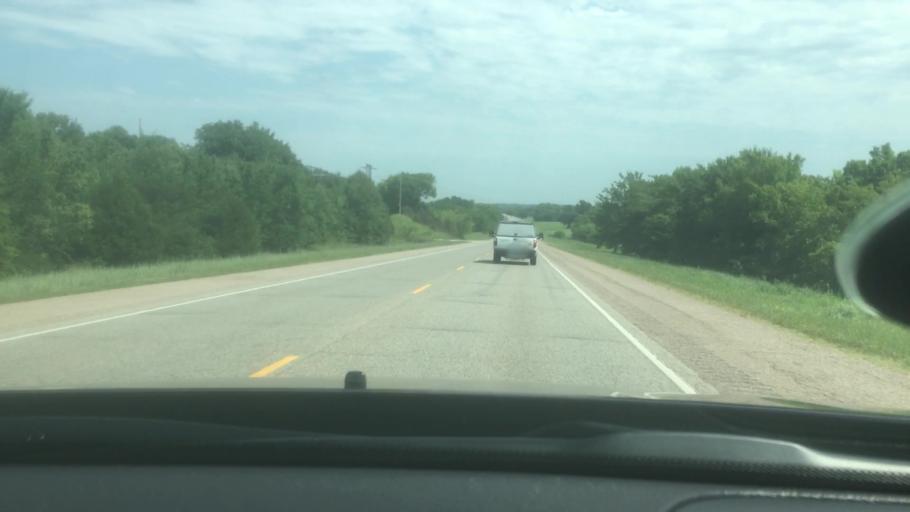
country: US
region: Oklahoma
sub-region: Seminole County
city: Maud
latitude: 35.0638
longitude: -96.9314
